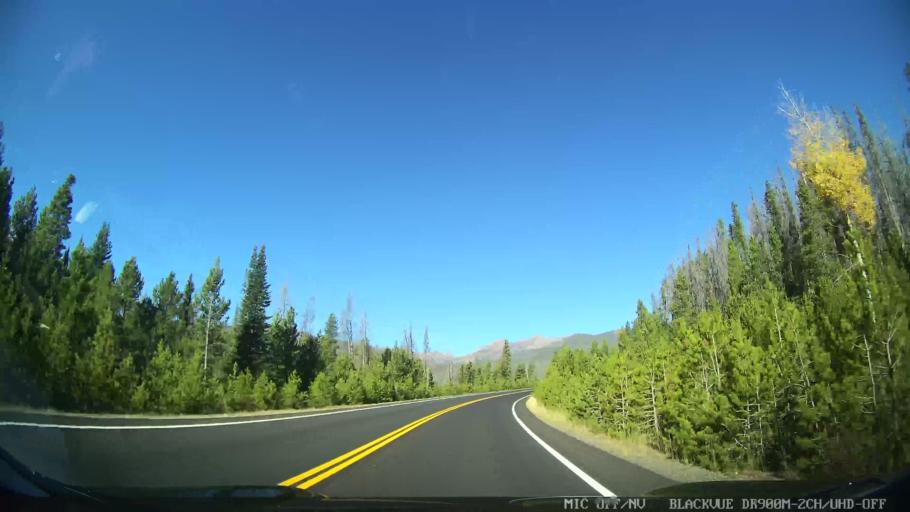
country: US
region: Colorado
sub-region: Grand County
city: Granby
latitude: 40.3201
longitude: -105.8503
